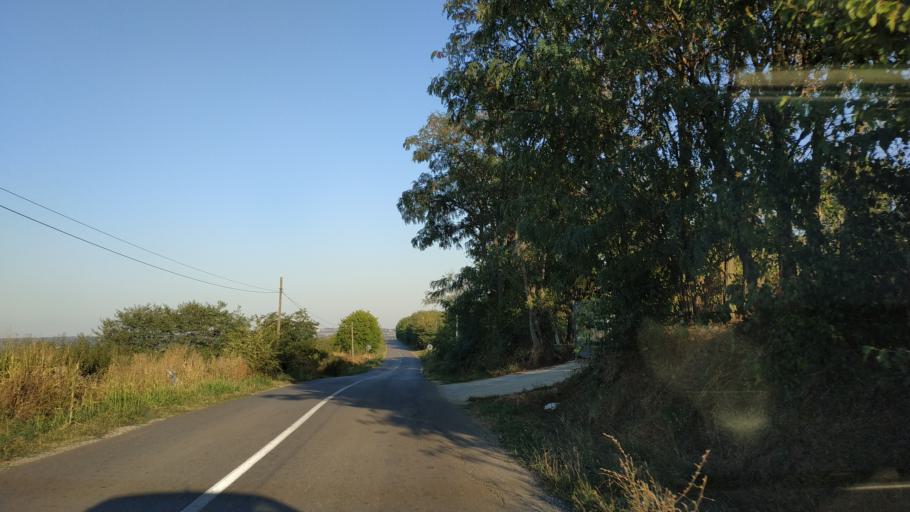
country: RS
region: Central Serbia
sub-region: Sumadijski Okrug
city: Topola
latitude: 44.2717
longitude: 20.6432
